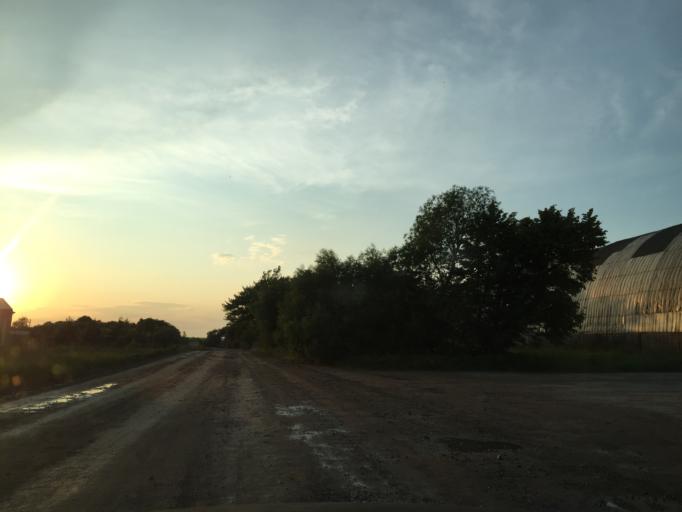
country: LT
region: Klaipedos apskritis
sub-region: Klaipeda
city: Klaipeda
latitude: 55.7543
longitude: 21.1530
